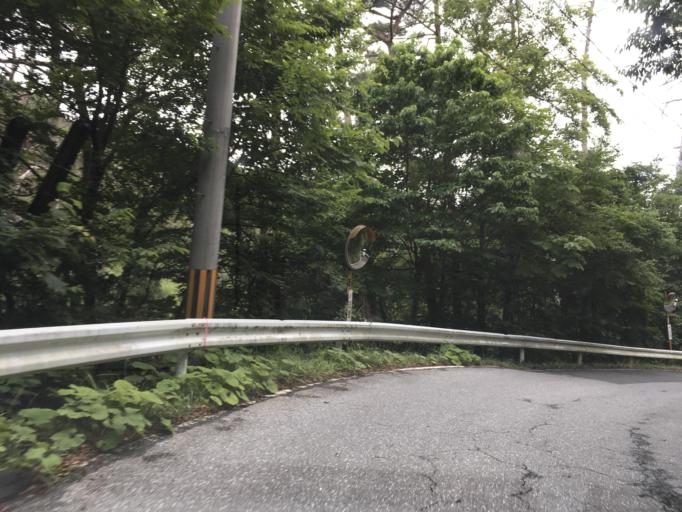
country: JP
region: Iwate
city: Ofunato
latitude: 38.9161
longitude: 141.6051
